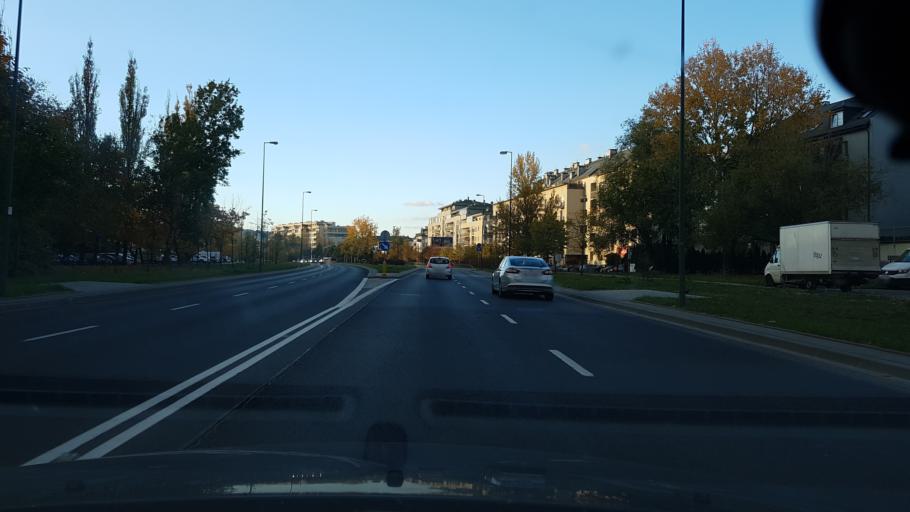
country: PL
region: Masovian Voivodeship
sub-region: Warszawa
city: Ursynow
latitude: 52.1509
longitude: 21.0584
